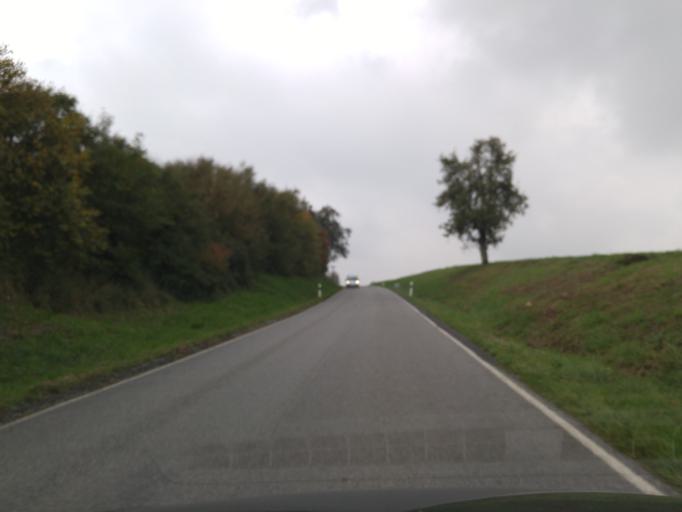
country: DE
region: Baden-Wuerttemberg
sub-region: Regierungsbezirk Stuttgart
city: Bad Rappenau
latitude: 49.2069
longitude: 9.0923
